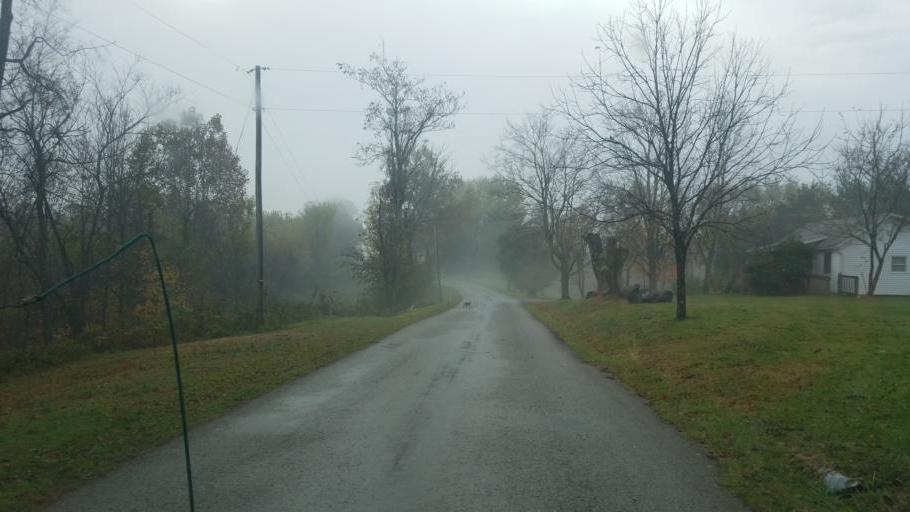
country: US
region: Ohio
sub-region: Morgan County
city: McConnelsville
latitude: 39.5041
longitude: -81.8242
